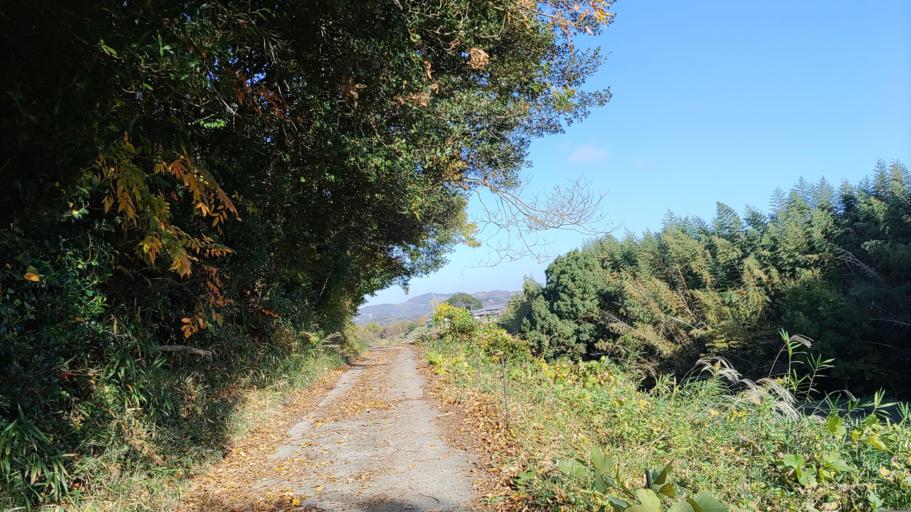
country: JP
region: Hyogo
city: Sumoto
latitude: 34.3826
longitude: 134.8176
